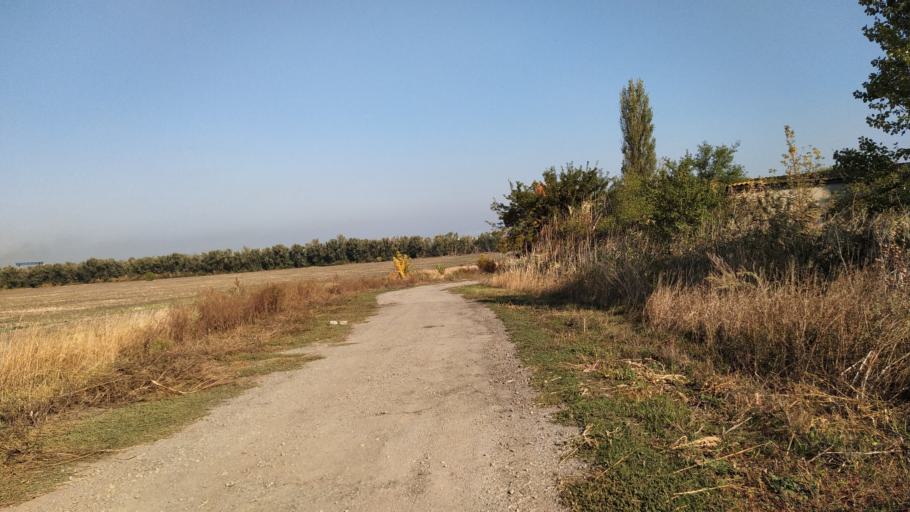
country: RU
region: Rostov
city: Bataysk
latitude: 47.0912
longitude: 39.7764
